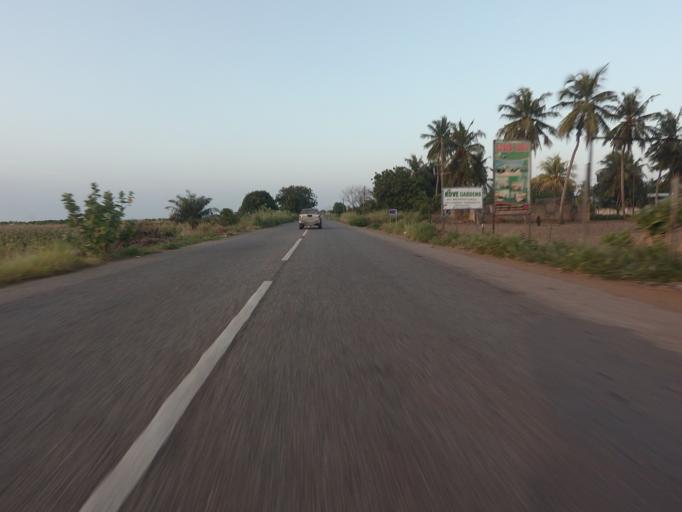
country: GH
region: Volta
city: Anloga
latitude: 5.8158
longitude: 0.9395
